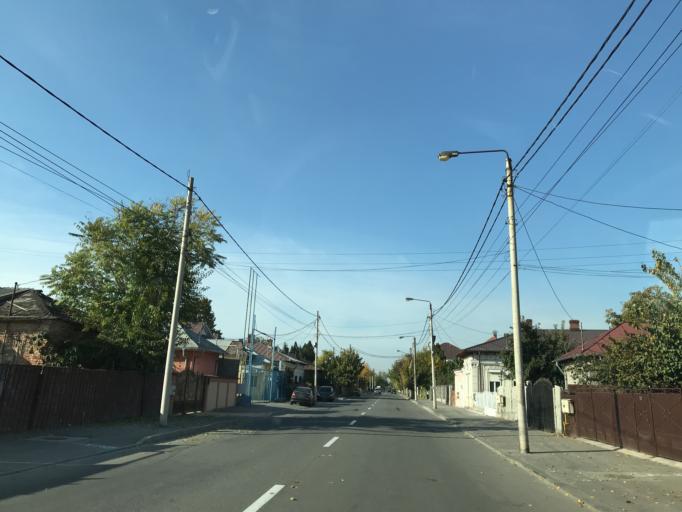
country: RO
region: Olt
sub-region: Municipiul Slatina
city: Slatina
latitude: 44.4355
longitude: 24.3498
